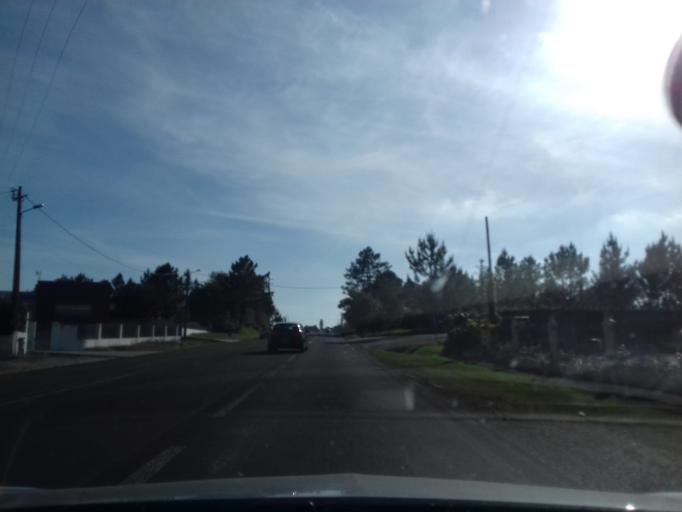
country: PT
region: Leiria
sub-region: Leiria
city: Leiria
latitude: 39.7132
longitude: -8.8383
